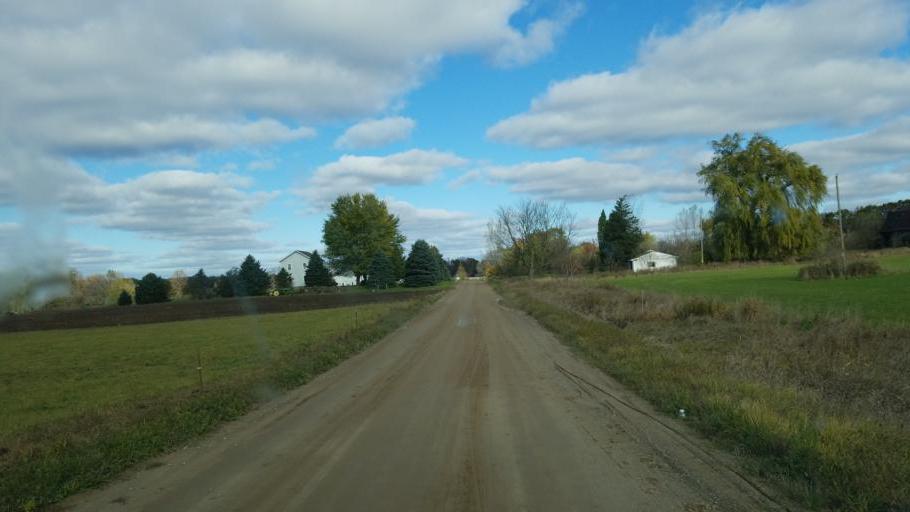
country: US
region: Michigan
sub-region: Montcalm County
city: Edmore
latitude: 43.5099
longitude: -84.9859
